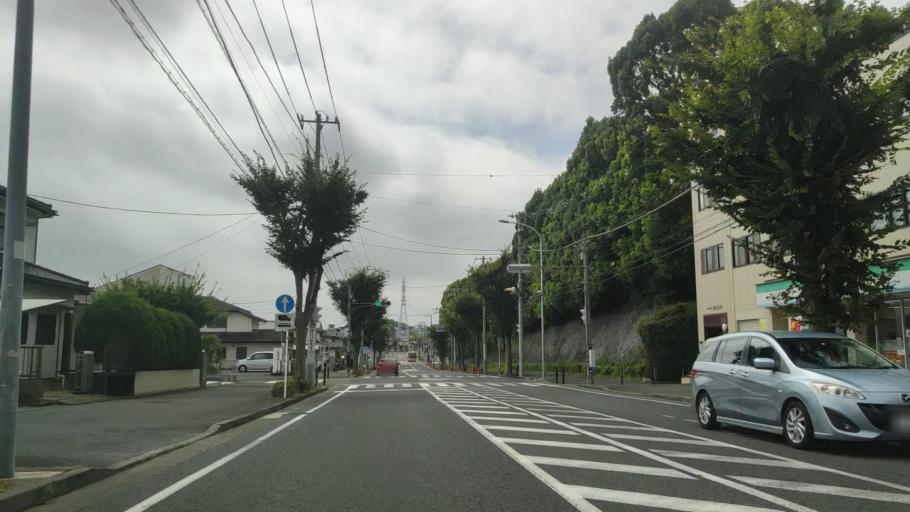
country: JP
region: Kanagawa
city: Fujisawa
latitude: 35.4145
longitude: 139.5222
